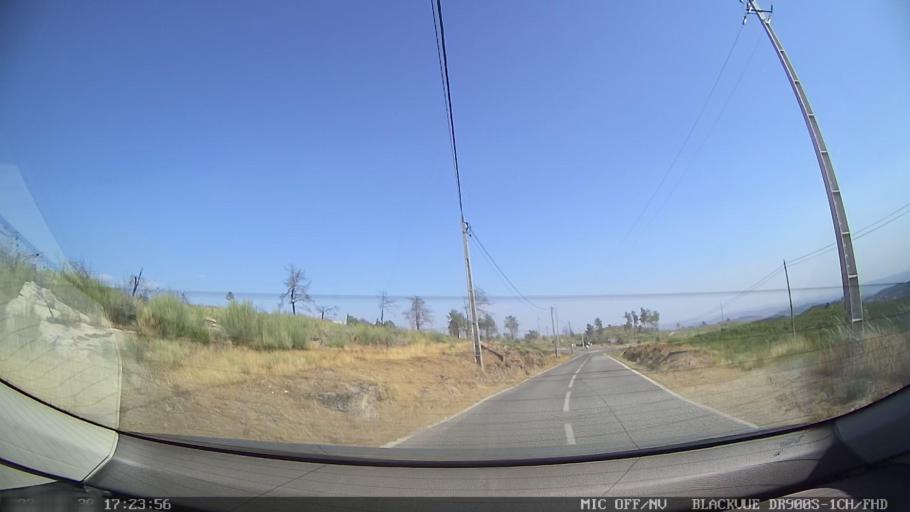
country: PT
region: Vila Real
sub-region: Murca
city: Murca
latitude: 41.3107
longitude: -7.4680
